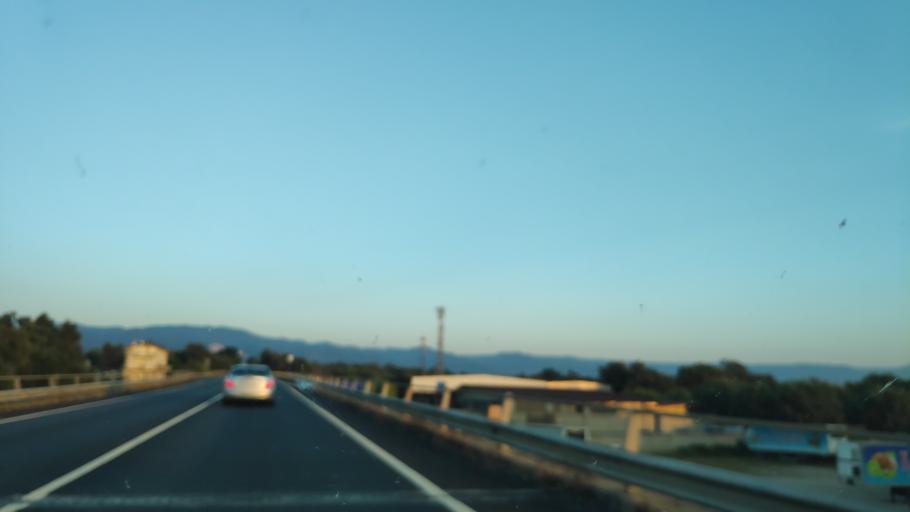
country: IT
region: Calabria
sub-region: Provincia di Reggio Calabria
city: Melicucco
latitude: 38.4337
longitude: 16.0500
